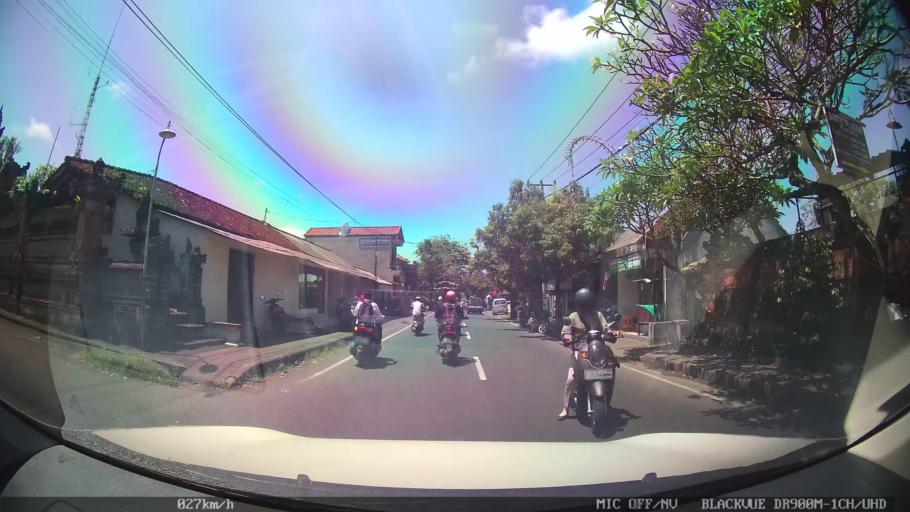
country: ID
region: Bali
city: Banjar Sedang
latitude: -8.5663
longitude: 115.3023
